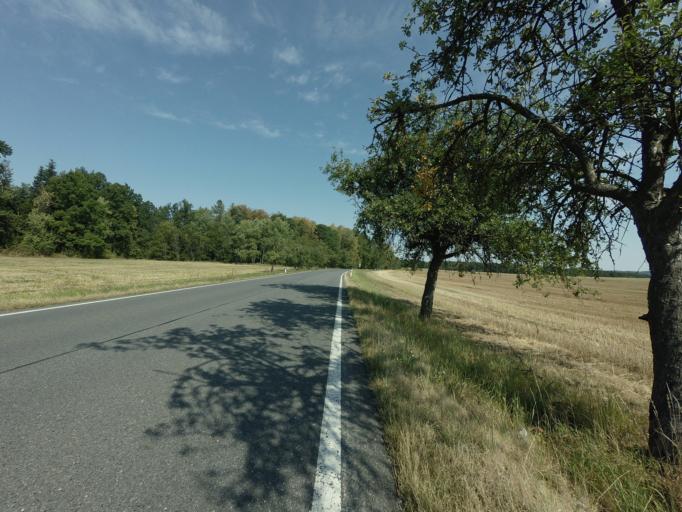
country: CZ
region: Jihocesky
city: Milevsko
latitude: 49.4162
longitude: 14.3582
